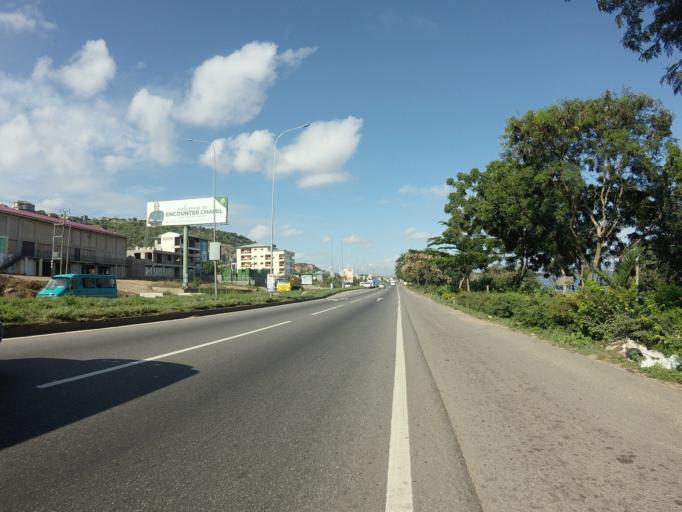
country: GH
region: Central
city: Kasoa
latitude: 5.5520
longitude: -0.3658
